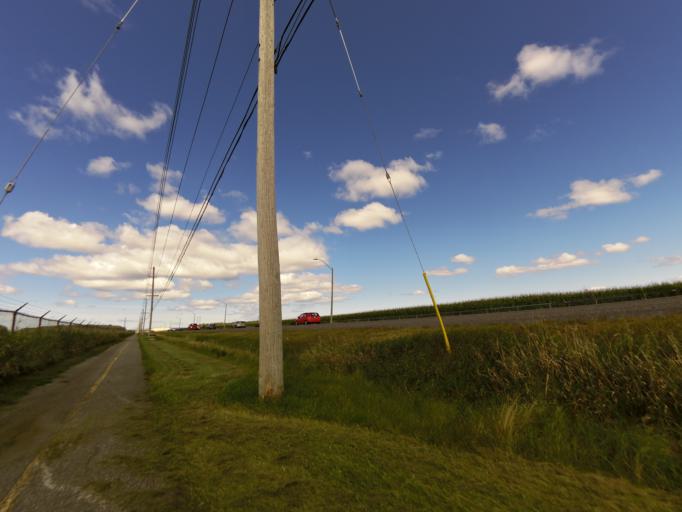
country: CA
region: Ontario
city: Bells Corners
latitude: 45.3061
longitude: -75.7676
